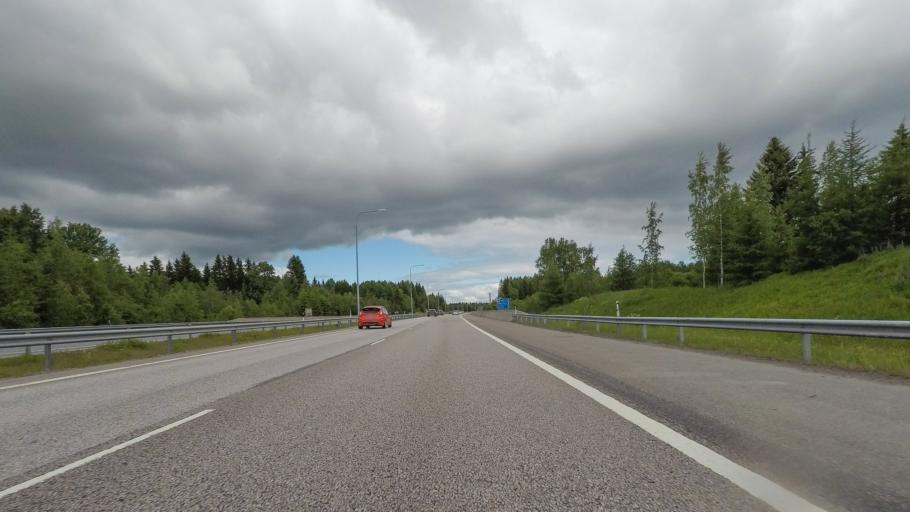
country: FI
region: Paijanne Tavastia
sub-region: Lahti
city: Lahti
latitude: 60.9218
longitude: 25.6284
